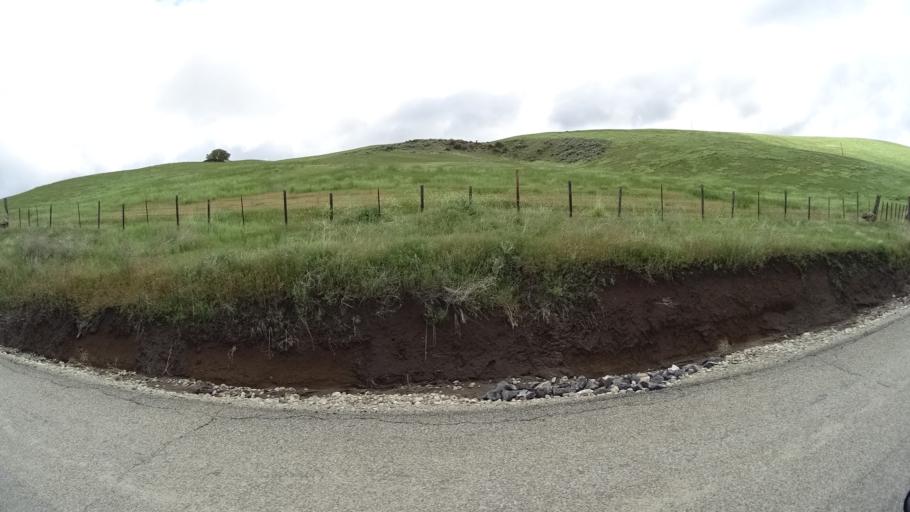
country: US
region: Idaho
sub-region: Ada County
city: Garden City
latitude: 43.7373
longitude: -116.2268
